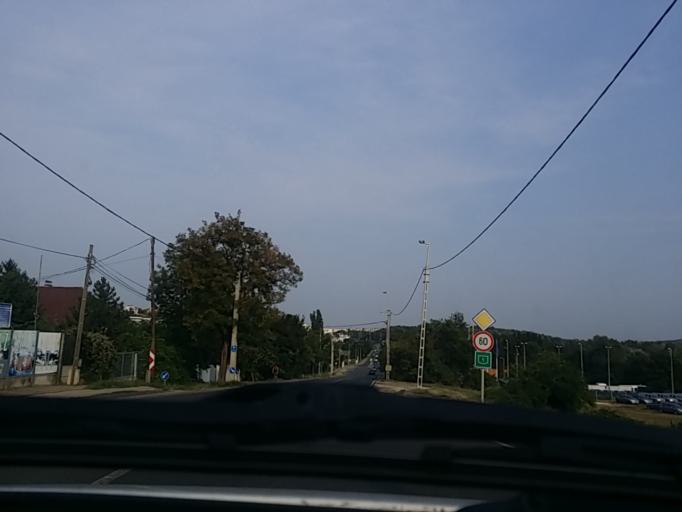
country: HU
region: Pest
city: Budaors
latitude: 47.4625
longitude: 18.9899
